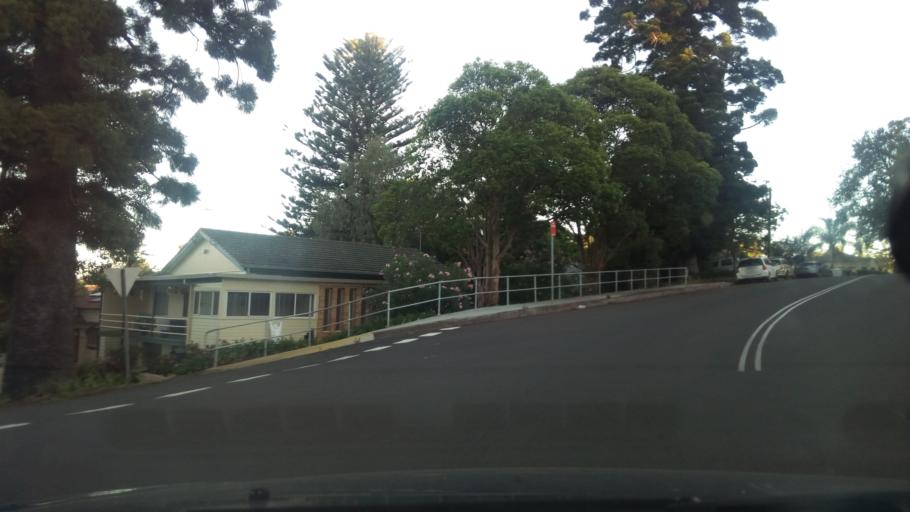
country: AU
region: New South Wales
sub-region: Wollongong
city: West Wollongong
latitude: -34.4272
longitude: 150.8732
